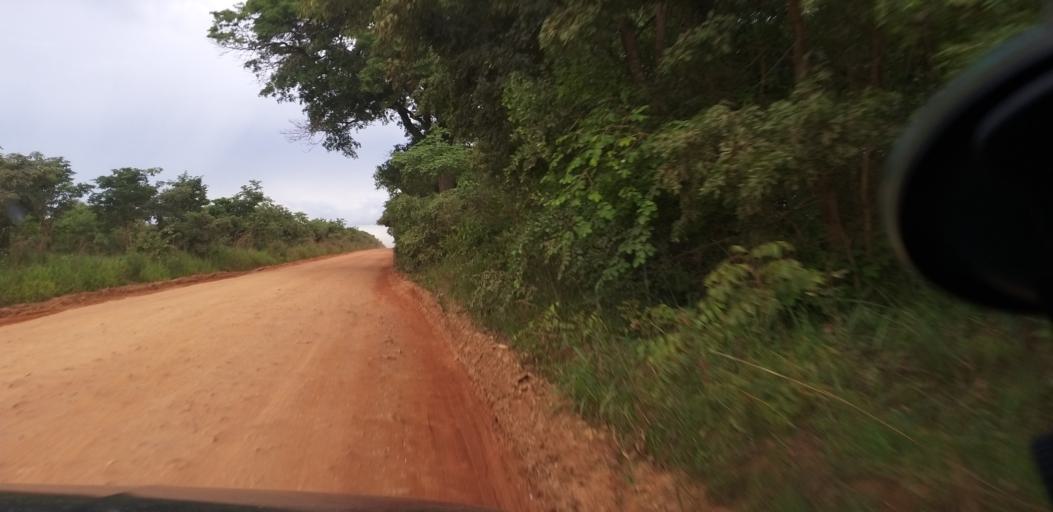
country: ZM
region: Lusaka
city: Lusaka
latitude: -15.2040
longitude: 28.4378
